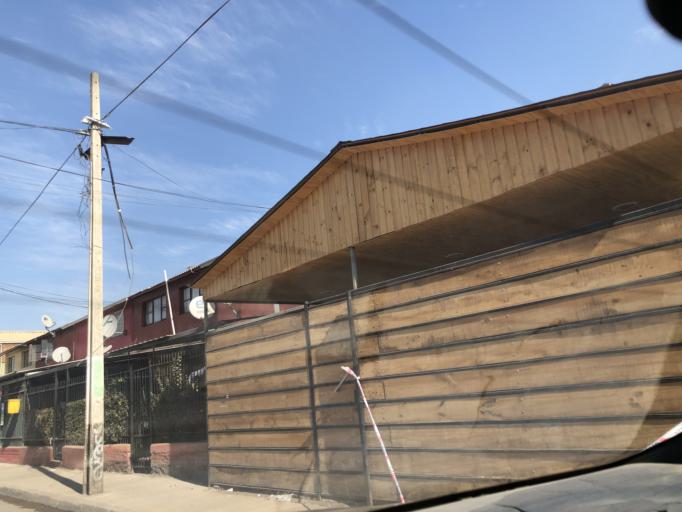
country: CL
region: Santiago Metropolitan
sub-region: Provincia de Santiago
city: La Pintana
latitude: -33.5895
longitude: -70.6056
